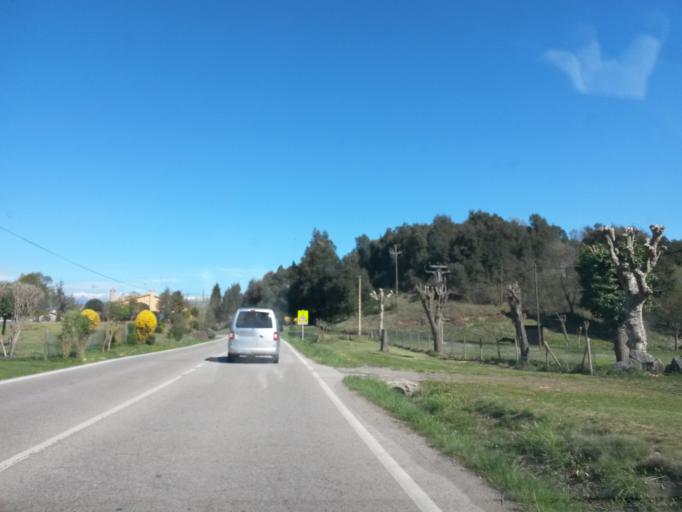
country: ES
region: Catalonia
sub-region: Provincia de Girona
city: Sant Cristofol de les Fonts
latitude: 42.1487
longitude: 2.5304
